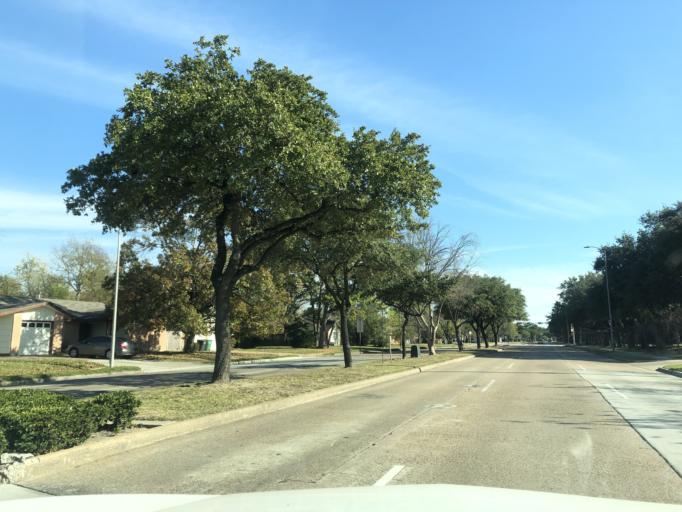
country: US
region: Texas
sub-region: Harris County
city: Bellaire
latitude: 29.6981
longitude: -95.5153
